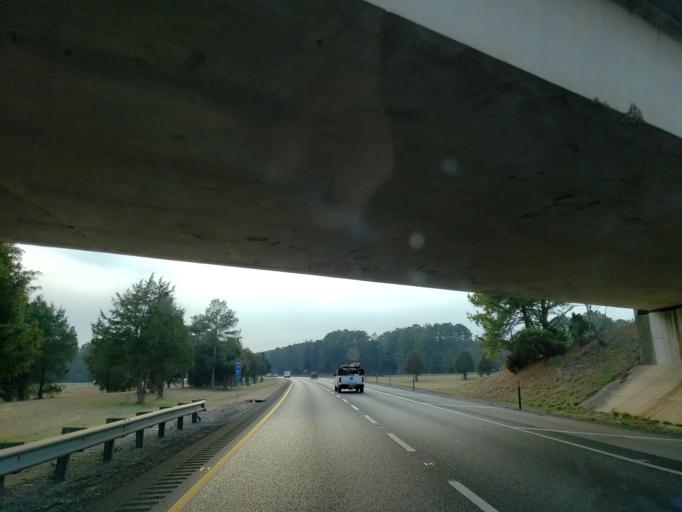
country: US
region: Tennessee
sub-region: Bradley County
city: Hopewell
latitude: 35.3253
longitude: -84.7831
